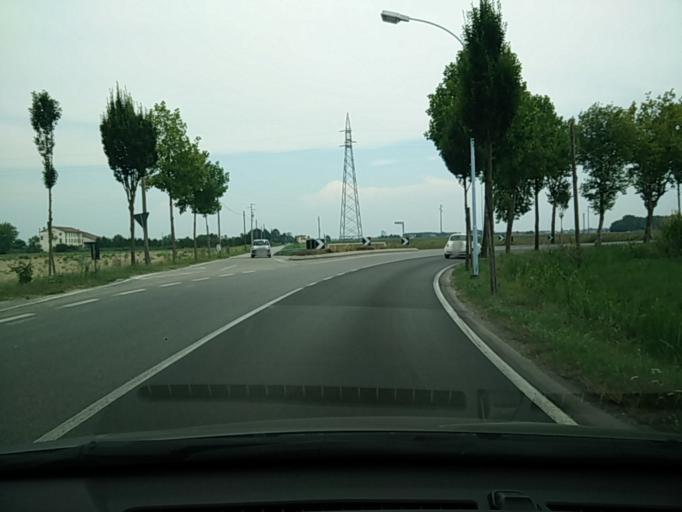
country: IT
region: Veneto
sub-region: Provincia di Venezia
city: Iesolo
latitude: 45.5348
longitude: 12.6522
